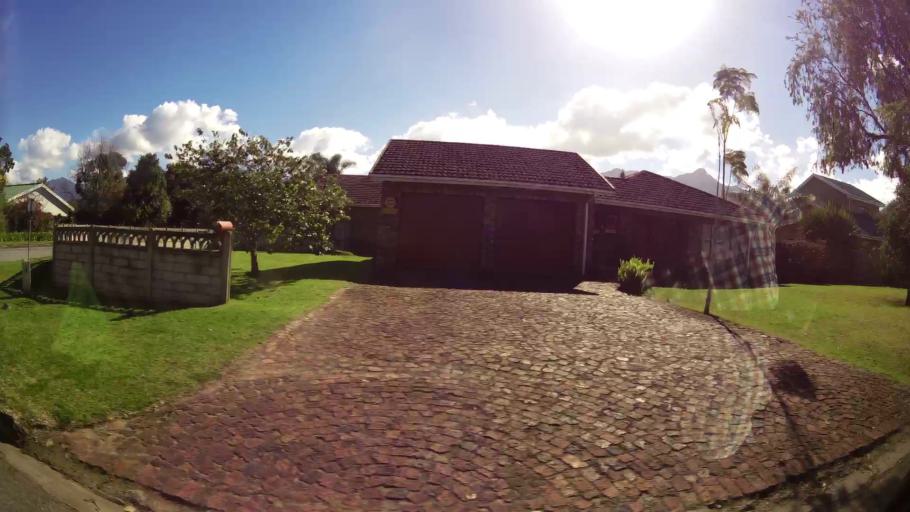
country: ZA
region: Western Cape
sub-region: Eden District Municipality
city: George
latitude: -33.9579
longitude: 22.4332
